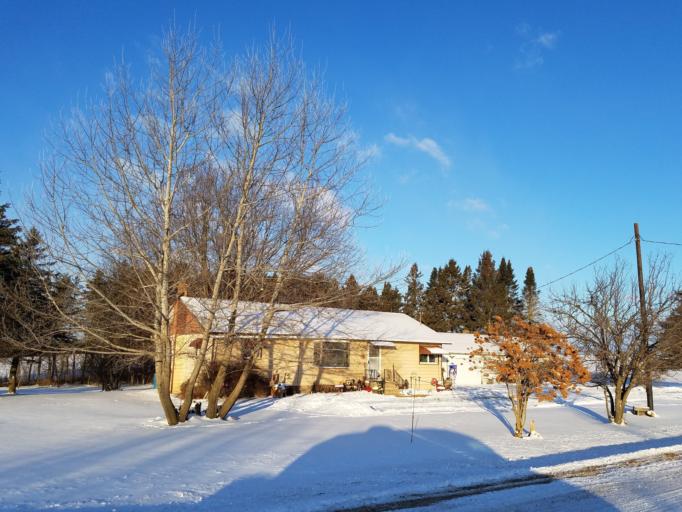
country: US
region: Wisconsin
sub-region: Clark County
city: Loyal
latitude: 44.6061
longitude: -90.4565
